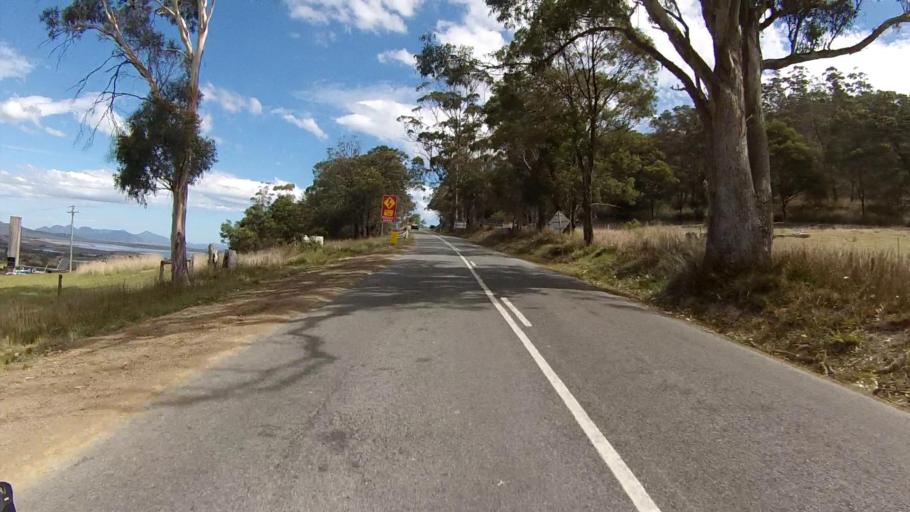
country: AU
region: Tasmania
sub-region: Break O'Day
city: St Helens
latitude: -41.9715
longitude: 148.1509
